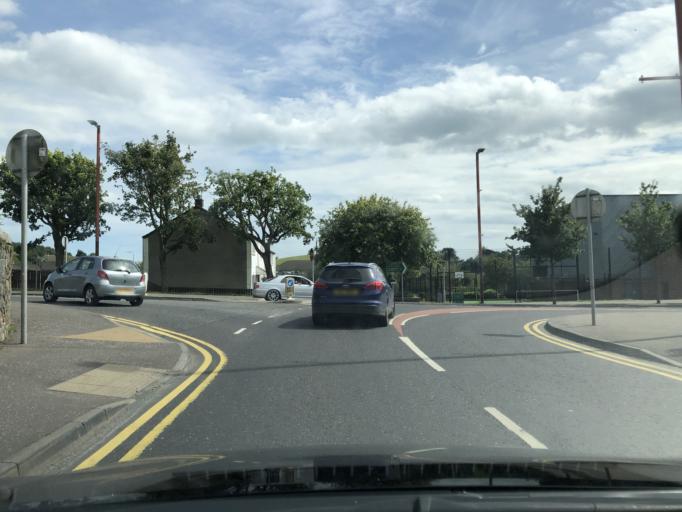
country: GB
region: Northern Ireland
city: Ballynahinch
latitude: 54.4029
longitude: -5.8938
